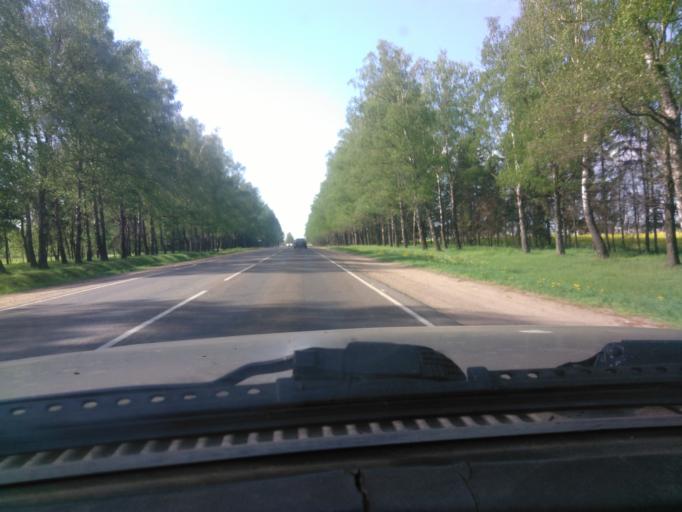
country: BY
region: Mogilev
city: Buynichy
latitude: 53.8457
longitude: 30.2508
